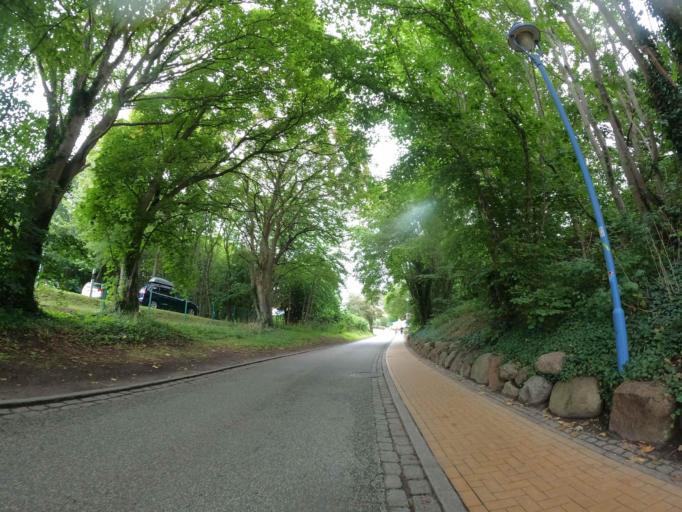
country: DE
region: Mecklenburg-Vorpommern
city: Ostseebad Gohren
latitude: 54.3371
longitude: 13.7401
